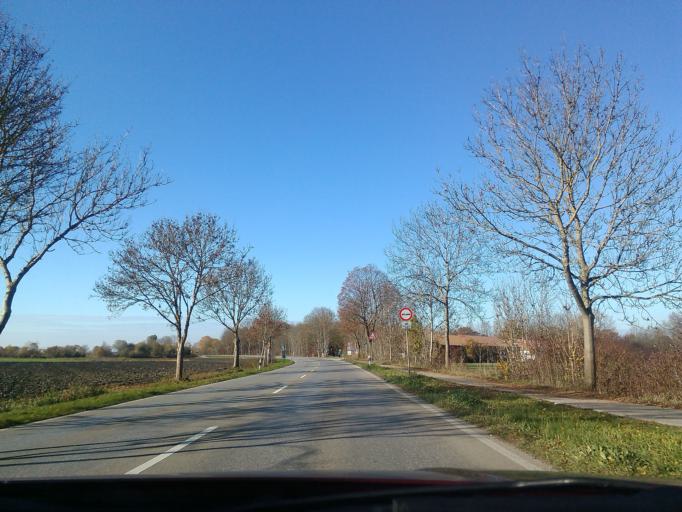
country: DE
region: Bavaria
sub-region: Upper Bavaria
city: Grobenzell
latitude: 48.1971
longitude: 11.3554
